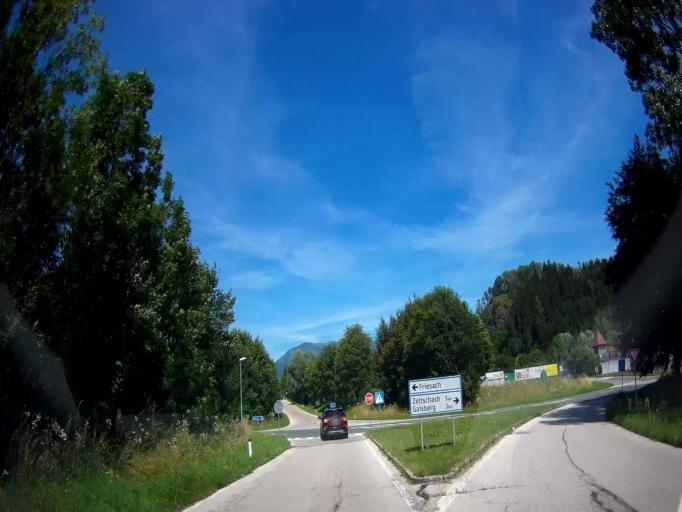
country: AT
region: Carinthia
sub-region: Politischer Bezirk Sankt Veit an der Glan
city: Friesach
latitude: 46.9523
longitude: 14.4187
